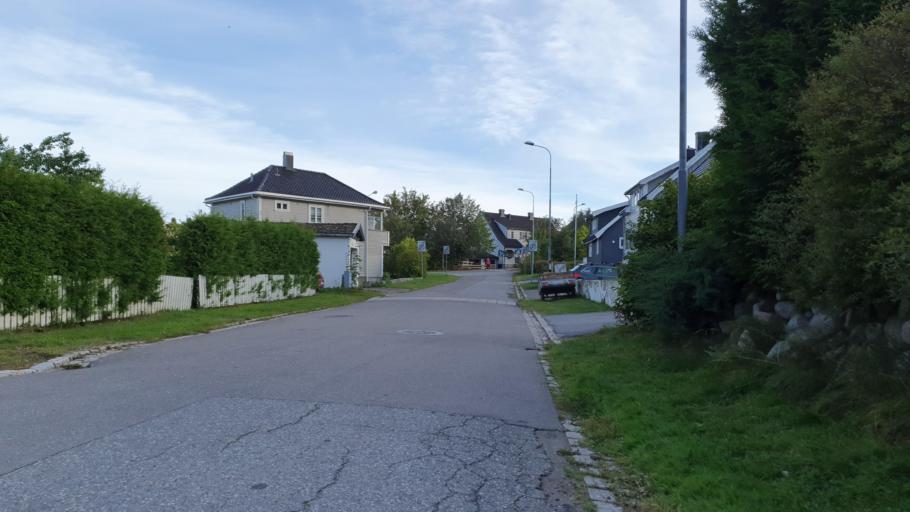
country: NO
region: Vestfold
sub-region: Tonsberg
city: Tonsberg
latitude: 59.2719
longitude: 10.4232
